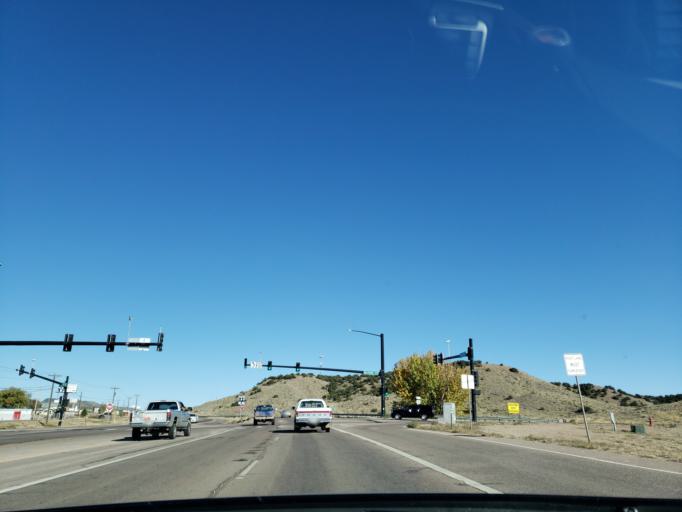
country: US
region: Colorado
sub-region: Fremont County
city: Lincoln Park
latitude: 38.4470
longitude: -105.1782
